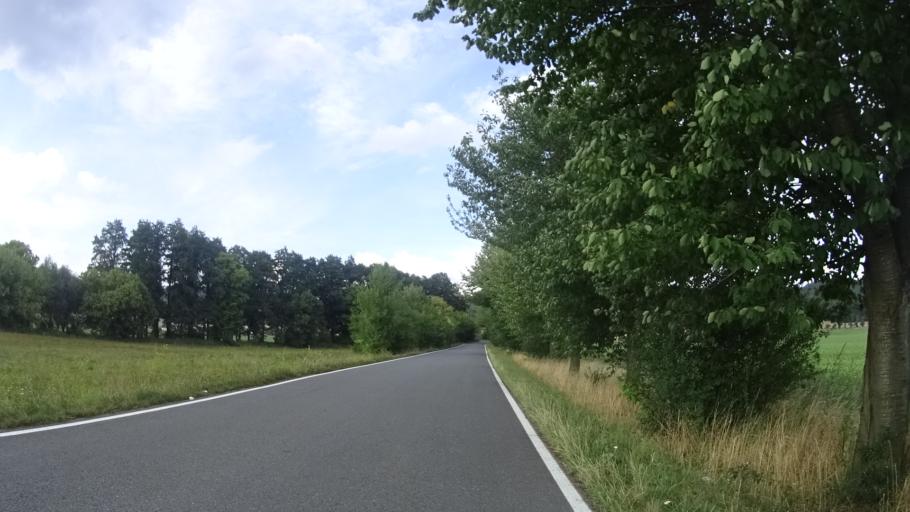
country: CZ
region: Olomoucky
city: Dubicko
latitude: 49.8416
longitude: 16.9424
